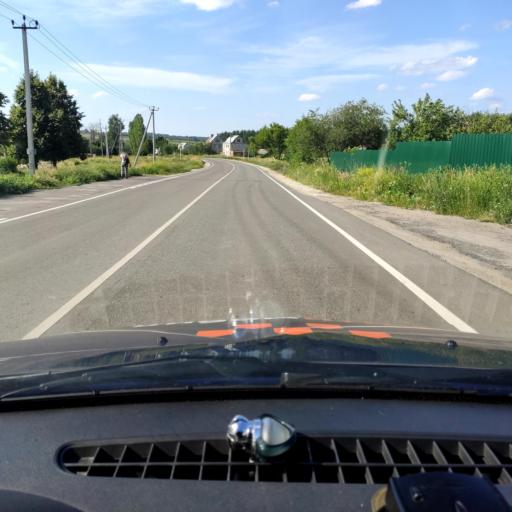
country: RU
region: Voronezj
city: Devitsa
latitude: 51.6504
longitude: 38.9727
